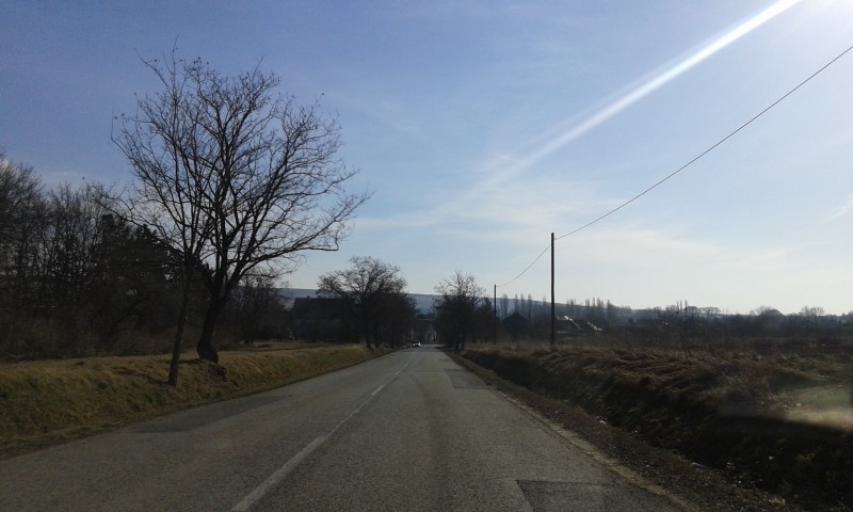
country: HU
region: Pest
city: Soskut
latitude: 47.4069
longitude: 18.8150
